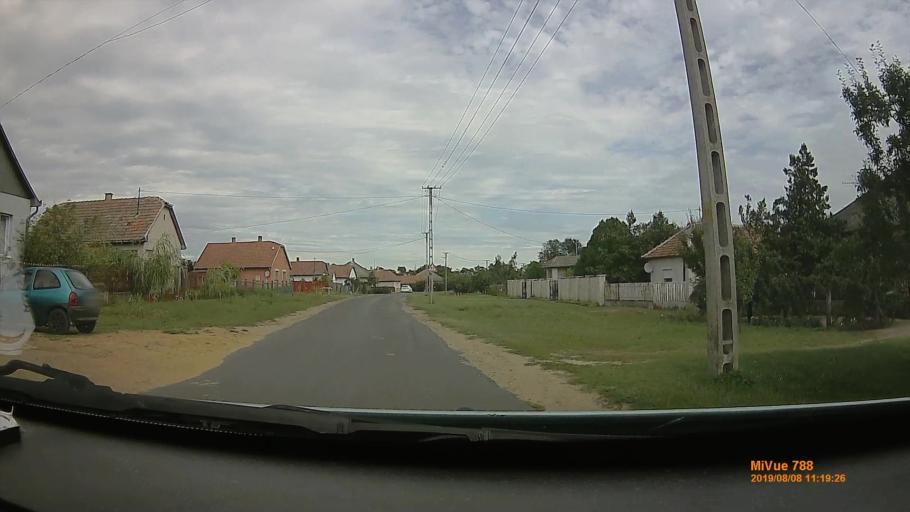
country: HU
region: Szabolcs-Szatmar-Bereg
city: Balkany
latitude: 47.7454
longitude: 21.8397
